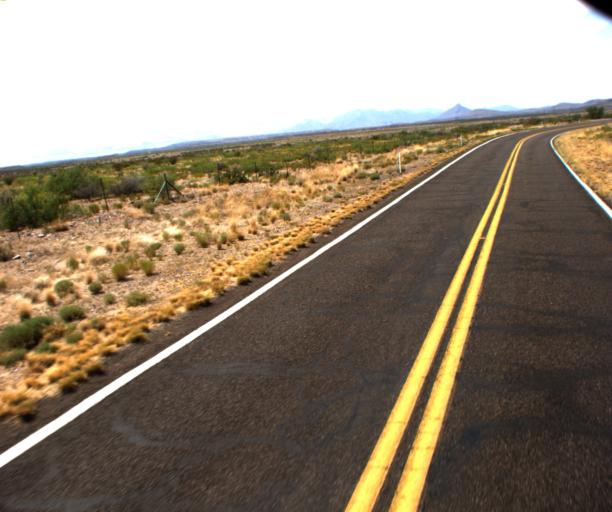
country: US
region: Arizona
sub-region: Greenlee County
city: Clifton
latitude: 32.9651
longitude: -109.2066
